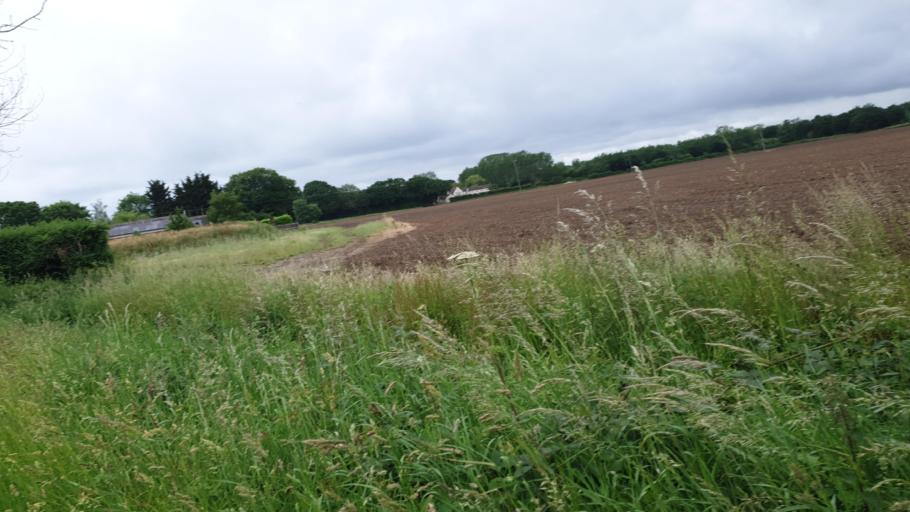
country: GB
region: England
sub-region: Essex
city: Great Bentley
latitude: 51.8779
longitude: 1.0419
